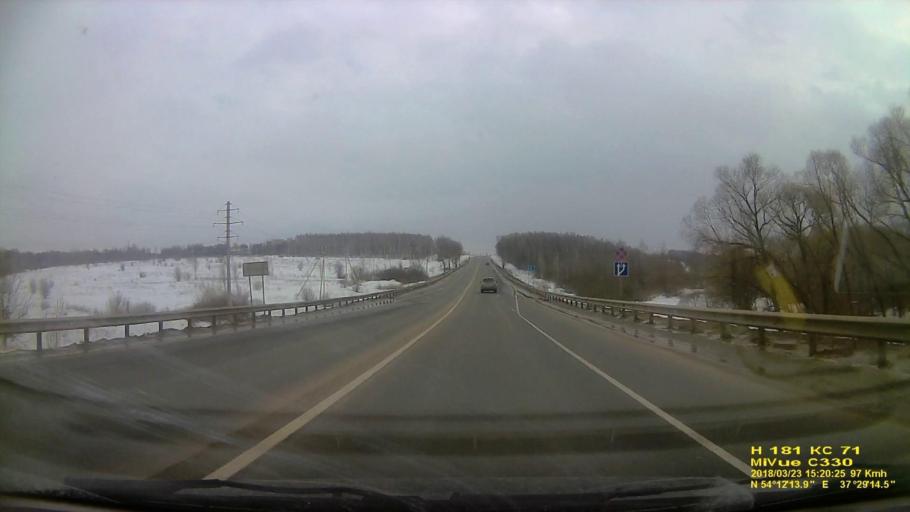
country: RU
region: Tula
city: Barsuki
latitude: 54.2044
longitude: 37.4882
